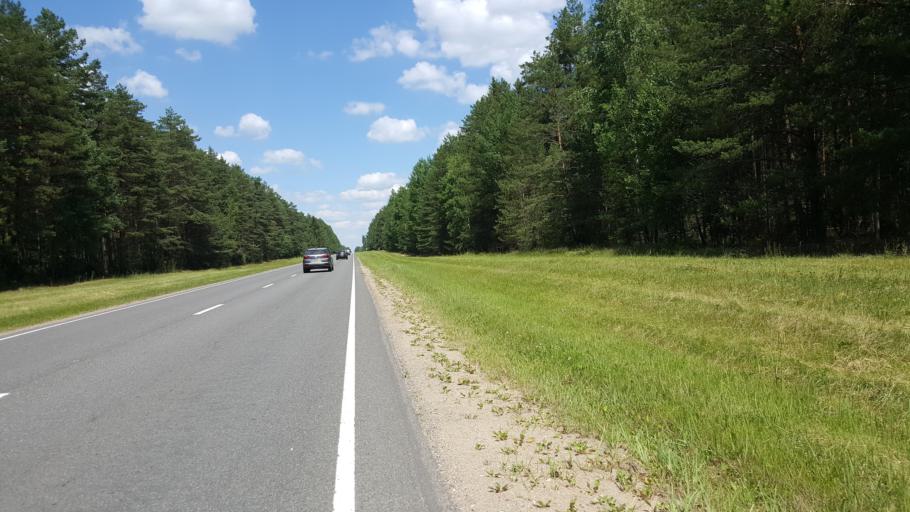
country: BY
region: Brest
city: Kamyanyuki
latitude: 52.5290
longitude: 23.7911
